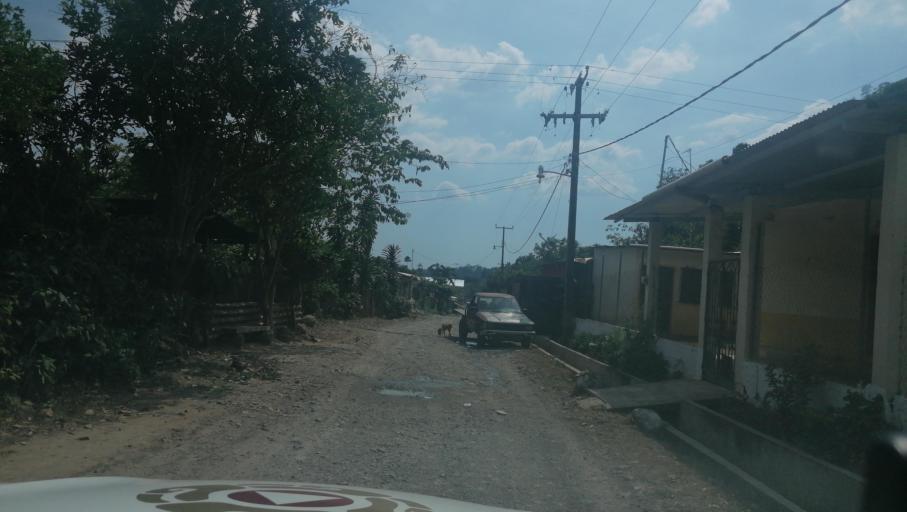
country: MX
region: Chiapas
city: Veinte de Noviembre
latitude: 15.0213
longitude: -92.2394
